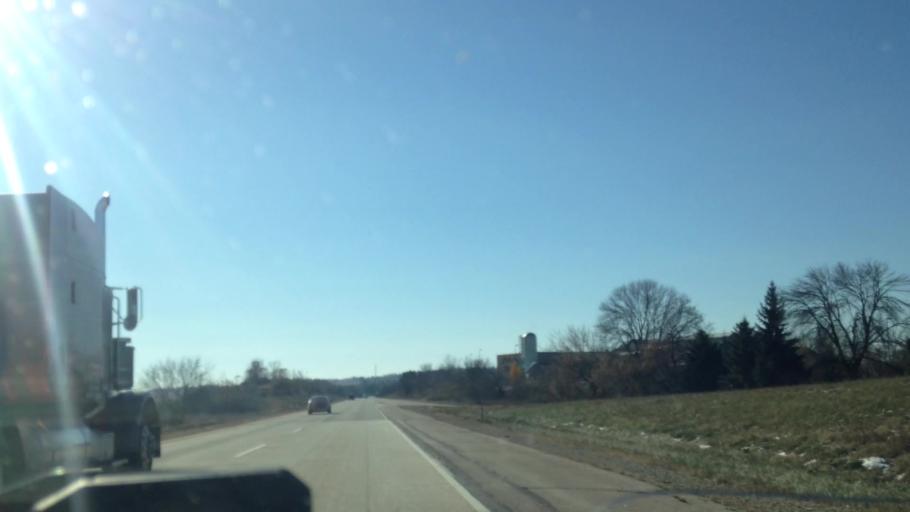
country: US
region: Wisconsin
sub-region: Washington County
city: Richfield
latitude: 43.2819
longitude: -88.1862
